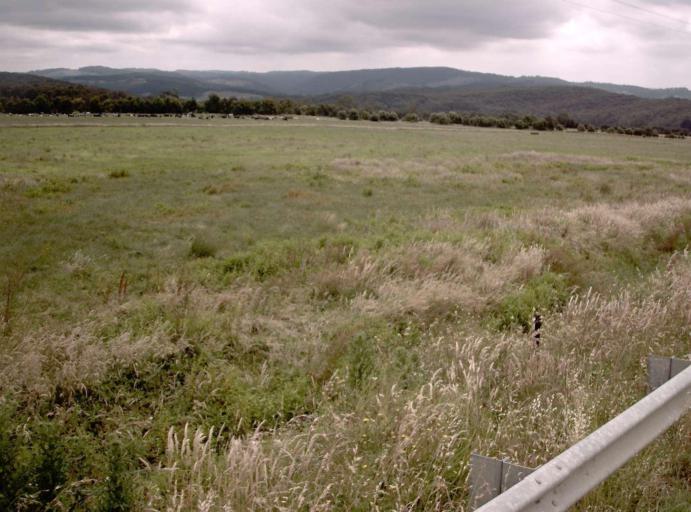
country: AU
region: Victoria
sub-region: Latrobe
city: Traralgon
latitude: -38.5080
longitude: 146.6635
